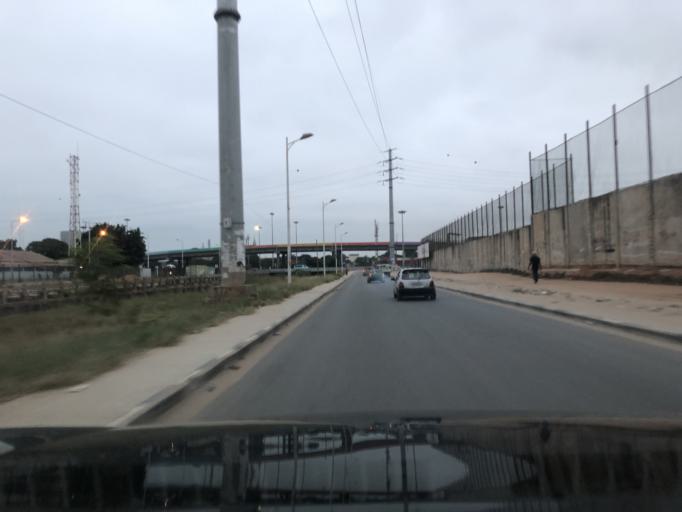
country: AO
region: Luanda
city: Luanda
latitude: -8.8363
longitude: 13.2553
